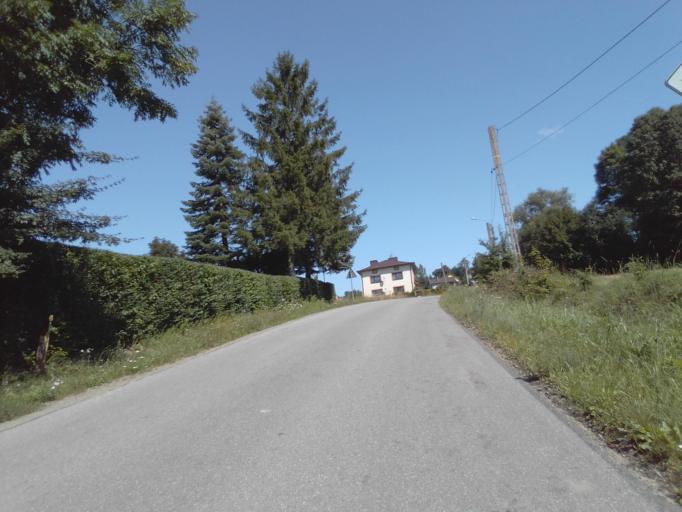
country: PL
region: Subcarpathian Voivodeship
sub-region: Powiat krosnienski
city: Jedlicze
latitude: 49.6743
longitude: 21.6113
